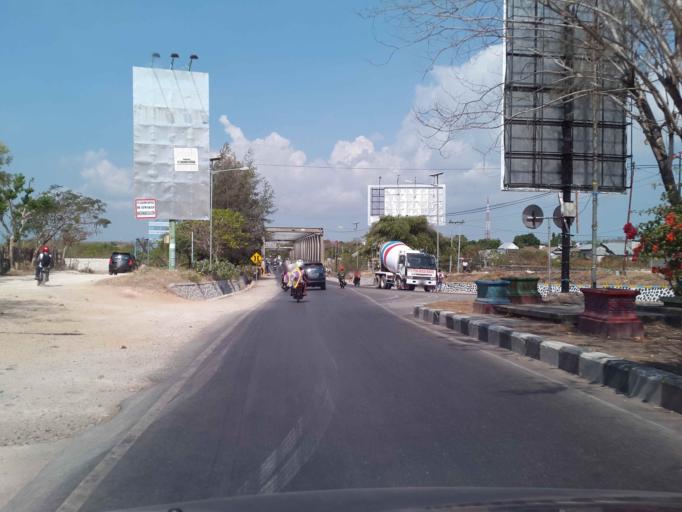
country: ID
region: East Nusa Tenggara
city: Oesapa
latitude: -10.1563
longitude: 123.6341
